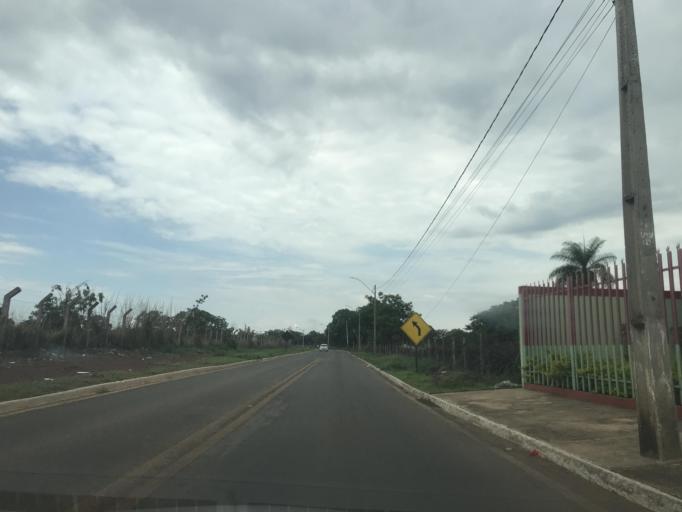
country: BR
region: Goias
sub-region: Luziania
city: Luziania
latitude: -16.2573
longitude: -47.9667
